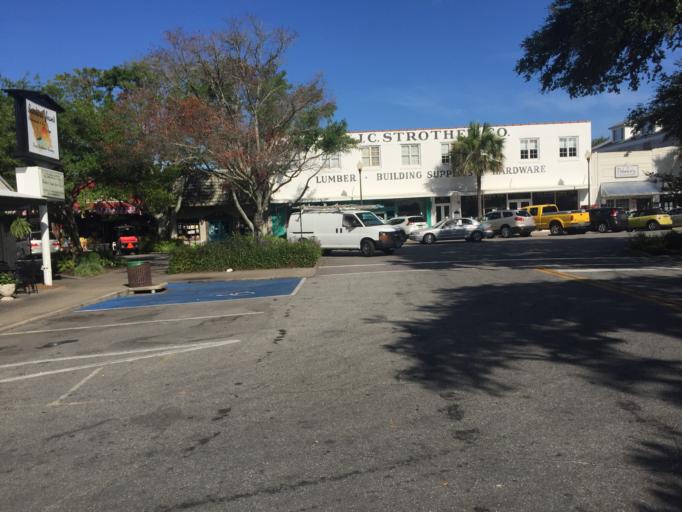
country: US
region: Georgia
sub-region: Glynn County
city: Saint Simons Island
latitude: 31.1356
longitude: -81.3957
